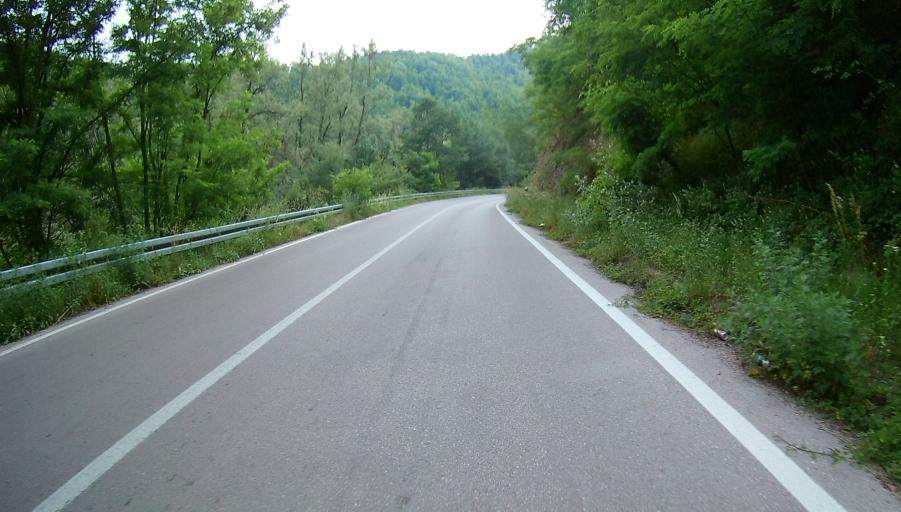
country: RS
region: Central Serbia
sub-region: Nisavski Okrug
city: Gadzin Han
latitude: 43.1710
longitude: 22.0727
